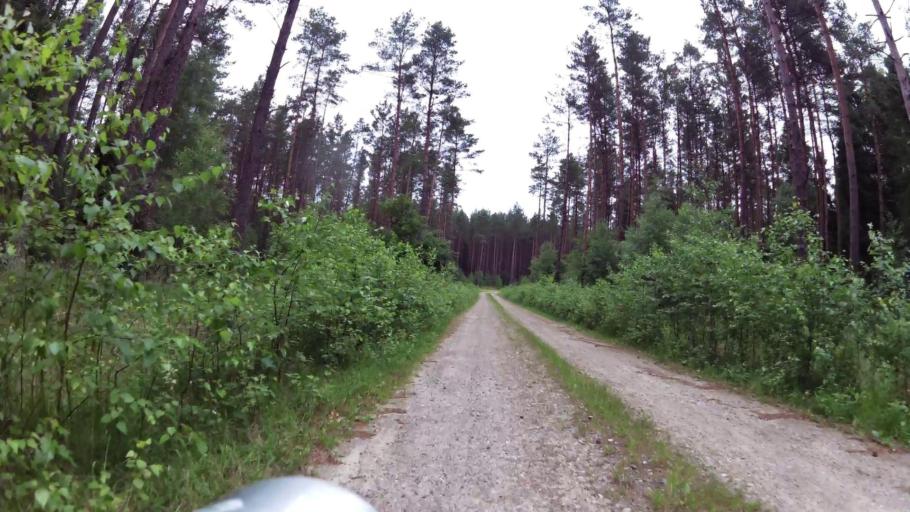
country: PL
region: West Pomeranian Voivodeship
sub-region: Powiat szczecinecki
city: Bialy Bor
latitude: 53.9197
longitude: 16.8314
